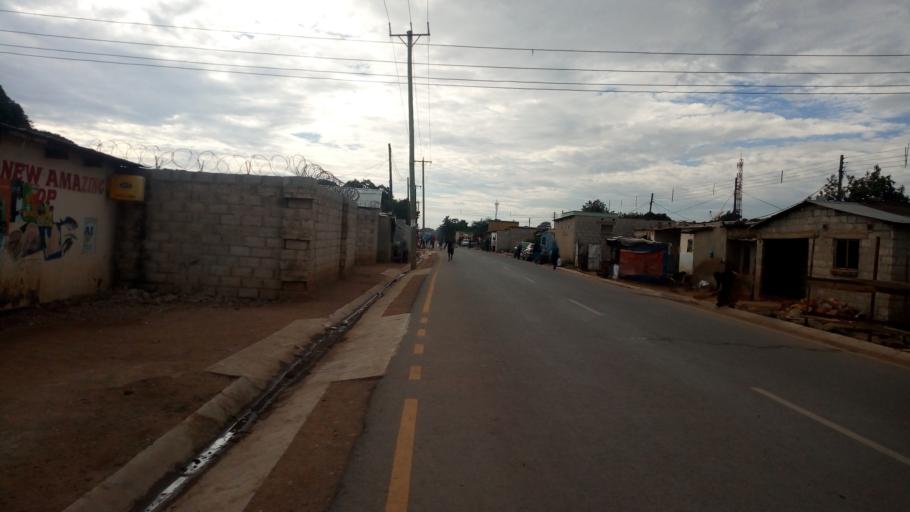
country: ZM
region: Lusaka
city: Lusaka
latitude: -15.3964
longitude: 28.2874
